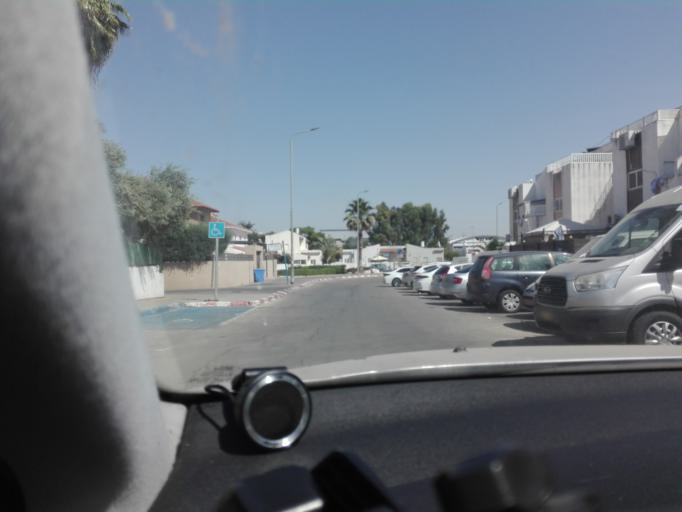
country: IL
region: Central District
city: Bene 'Ayish
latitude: 31.7263
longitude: 34.7463
